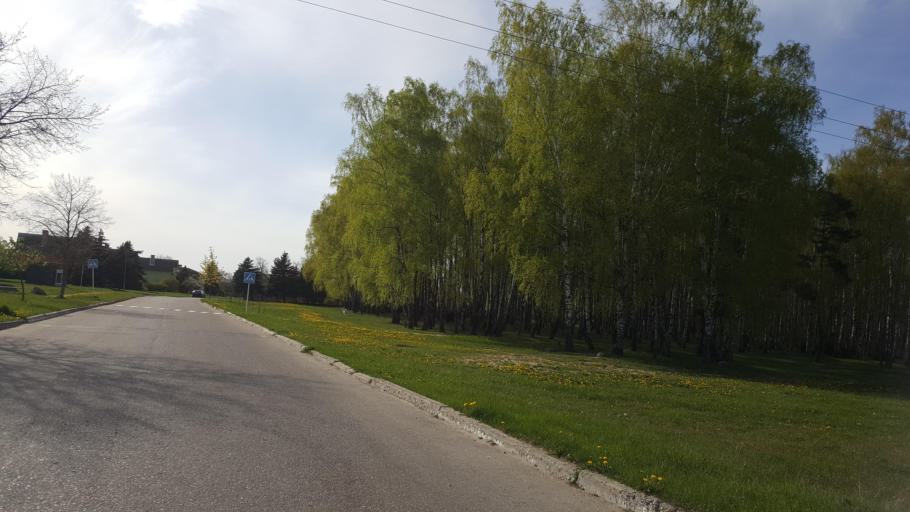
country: BY
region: Brest
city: Vysokaye
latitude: 52.3977
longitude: 23.4633
